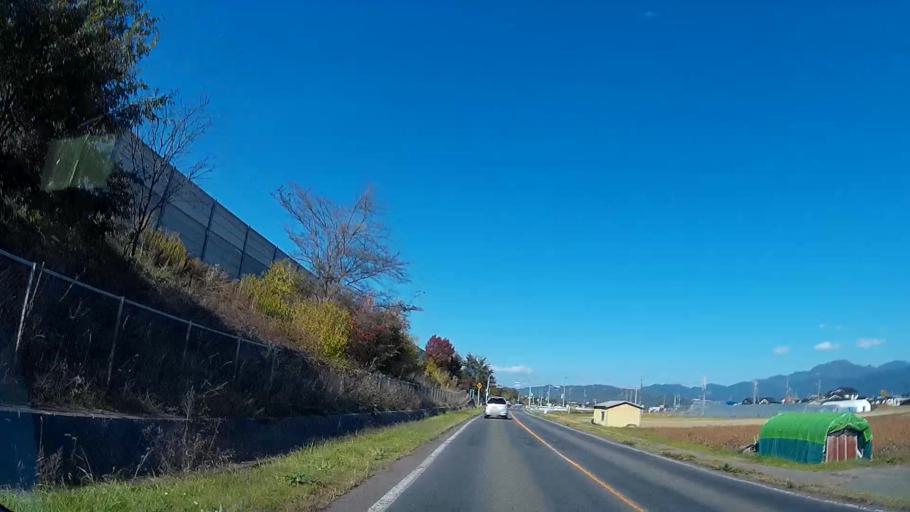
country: JP
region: Nagano
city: Matsumoto
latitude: 36.2135
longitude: 137.9304
